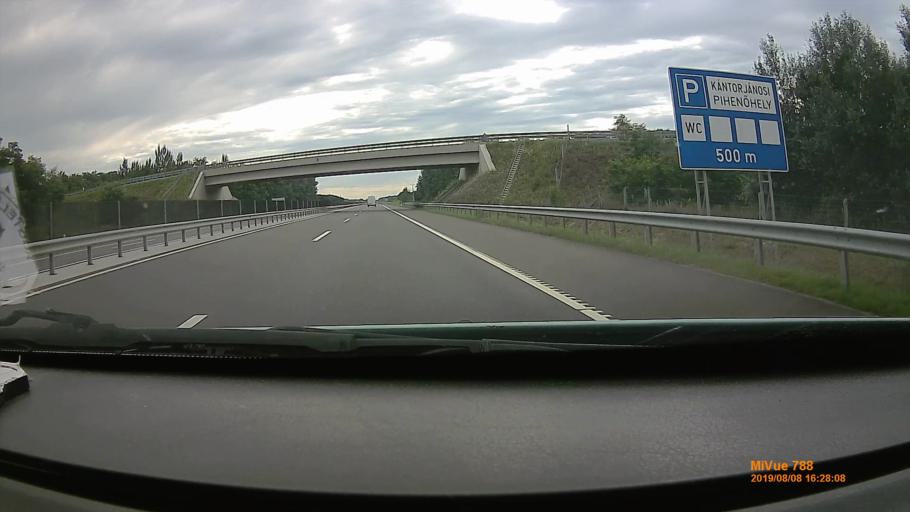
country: HU
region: Szabolcs-Szatmar-Bereg
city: Kantorjanosi
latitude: 47.9605
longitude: 22.1754
